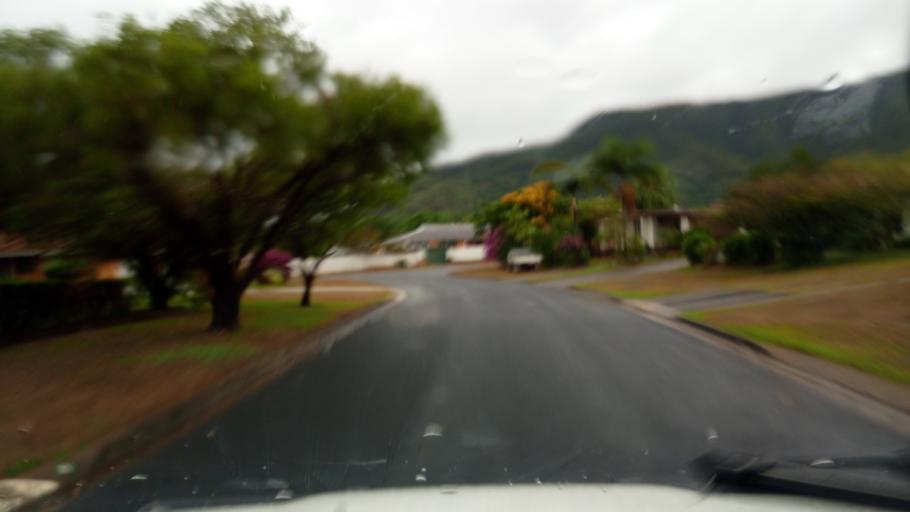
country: AU
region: Queensland
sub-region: Cairns
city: Woree
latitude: -16.9573
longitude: 145.7294
